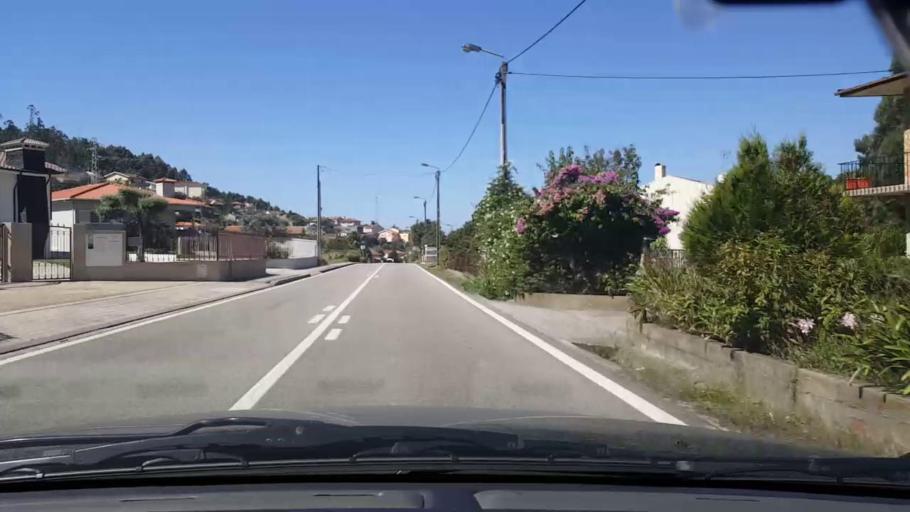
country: PT
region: Braga
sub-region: Vila Nova de Famalicao
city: Ribeirao
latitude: 41.3376
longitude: -8.6328
